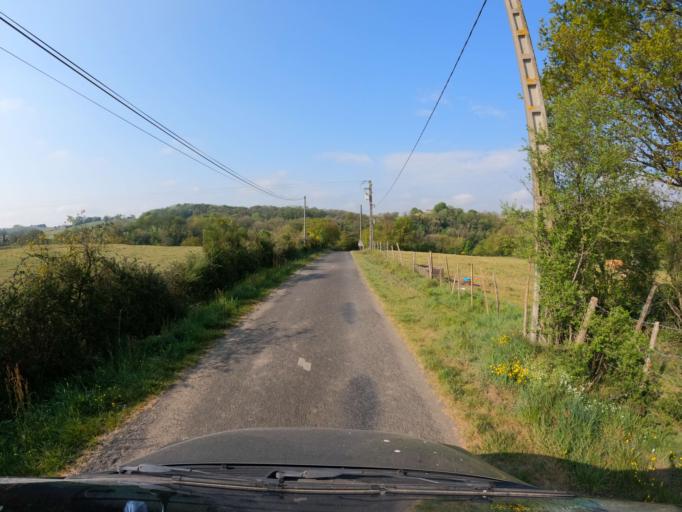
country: FR
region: Pays de la Loire
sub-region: Departement de Maine-et-Loire
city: La Romagne
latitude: 47.0690
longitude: -1.0074
